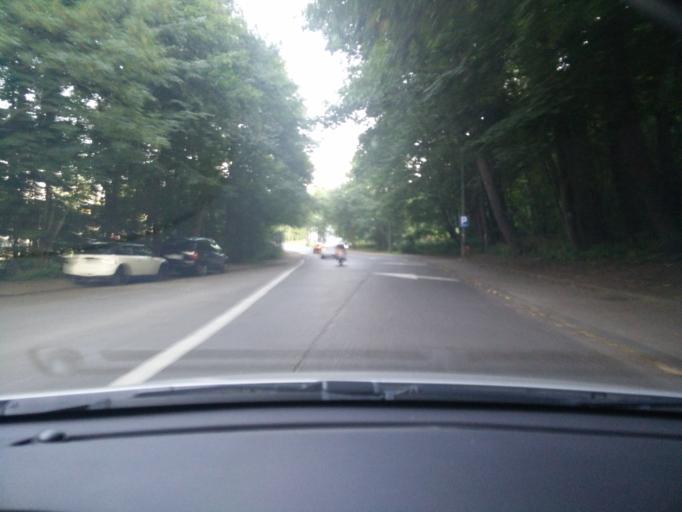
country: PL
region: Pomeranian Voivodeship
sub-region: Sopot
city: Sopot
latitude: 54.4534
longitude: 18.5603
